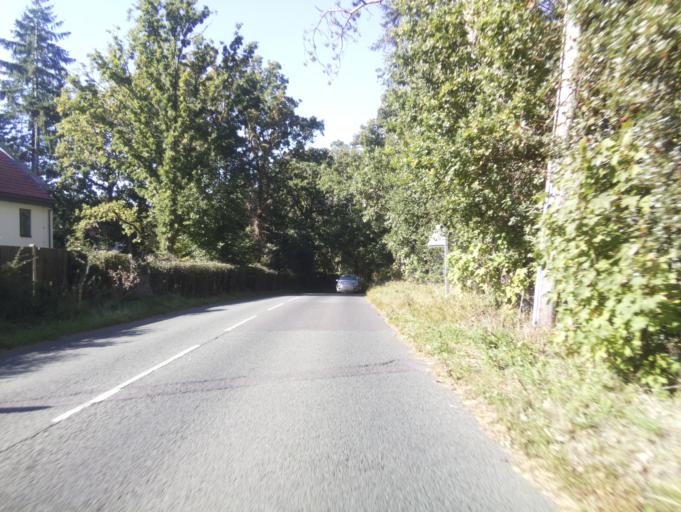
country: GB
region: England
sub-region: West Berkshire
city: Hermitage
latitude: 51.4394
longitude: -1.2741
